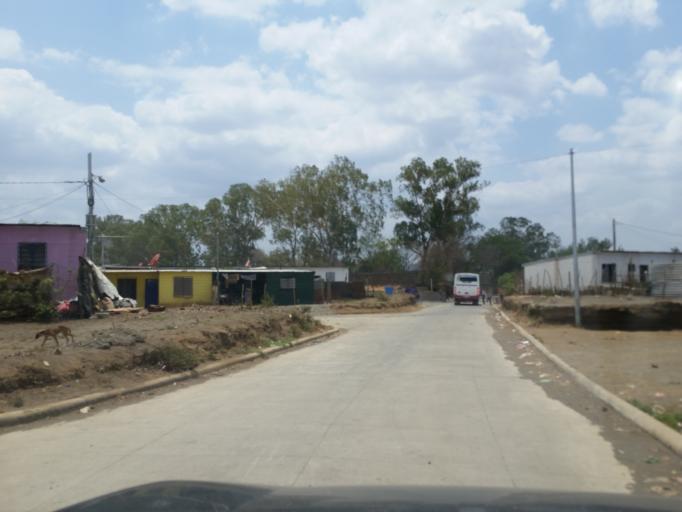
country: NI
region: Managua
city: Managua
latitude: 12.1295
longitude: -86.1589
